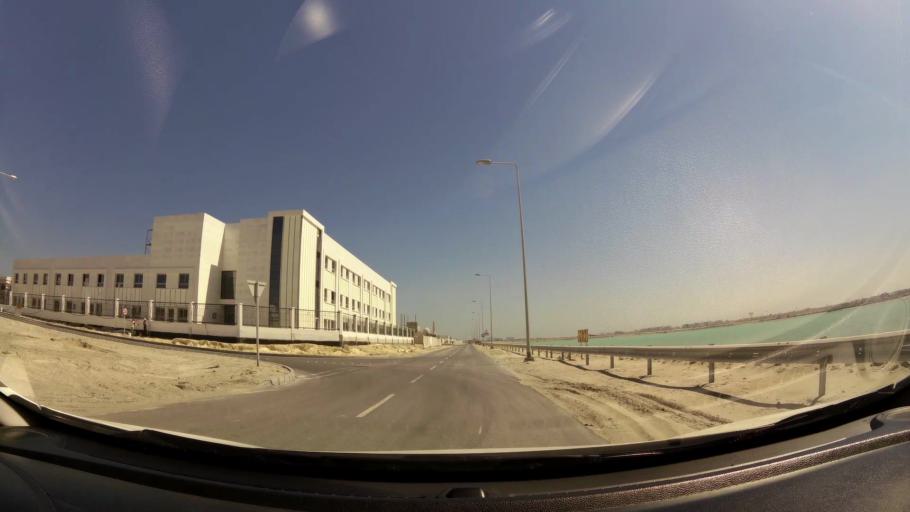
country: BH
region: Muharraq
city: Al Muharraq
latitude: 26.2989
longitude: 50.6350
